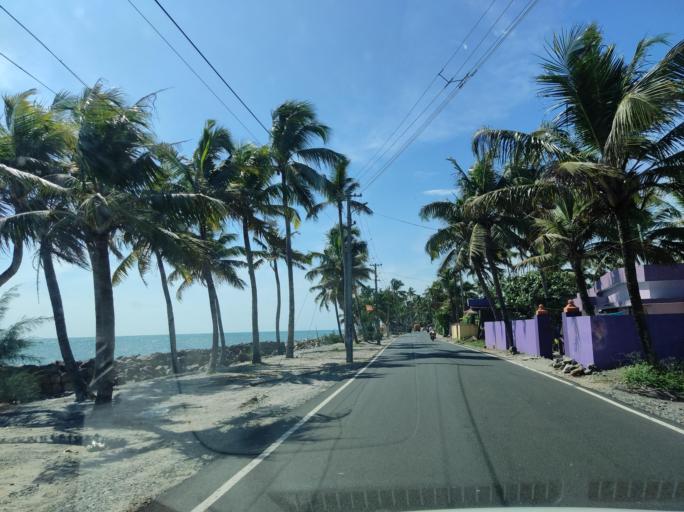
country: IN
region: Kerala
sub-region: Alappuzha
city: Kayankulam
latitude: 9.2523
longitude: 76.4101
